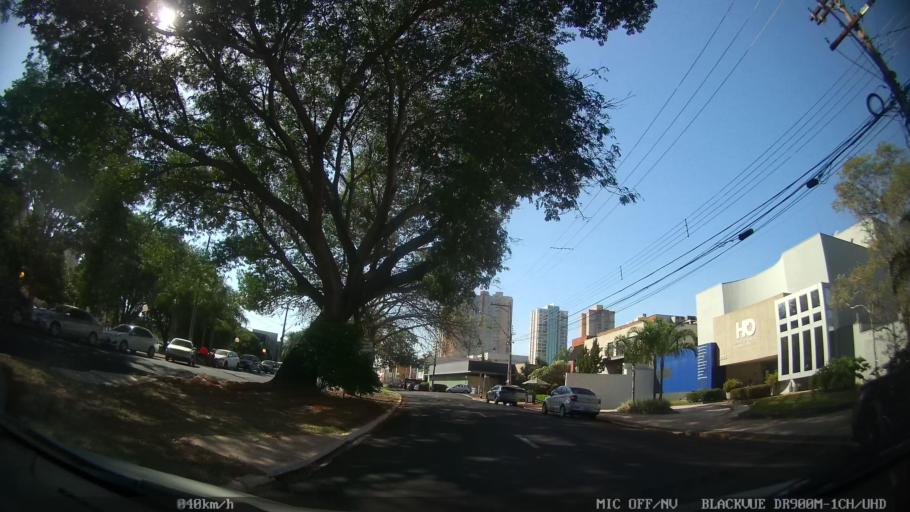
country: BR
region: Sao Paulo
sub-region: Ribeirao Preto
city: Ribeirao Preto
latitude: -21.2122
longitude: -47.8086
